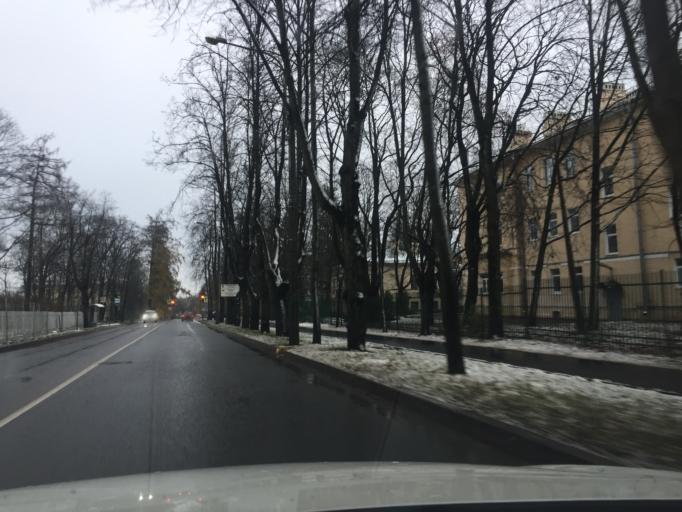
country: RU
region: St.-Petersburg
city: Pushkin
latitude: 59.7116
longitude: 30.4088
